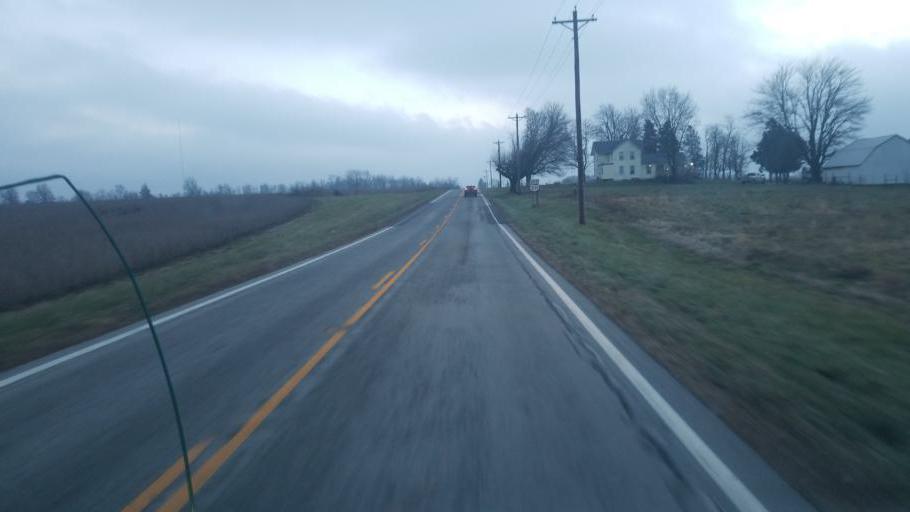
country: US
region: Ohio
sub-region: Wyandot County
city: Upper Sandusky
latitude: 40.9252
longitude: -83.1313
